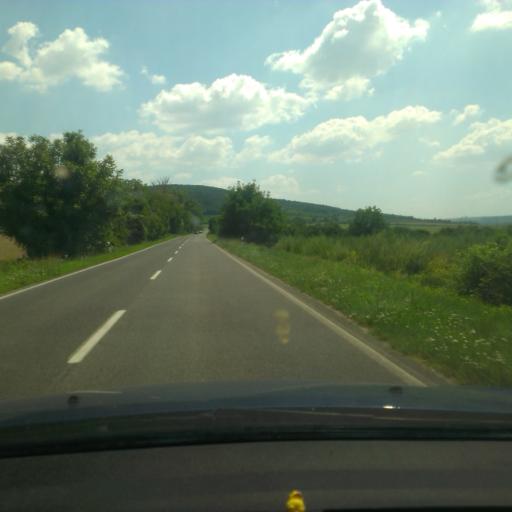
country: SK
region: Trnavsky
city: Hlohovec
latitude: 48.4680
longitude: 17.8121
